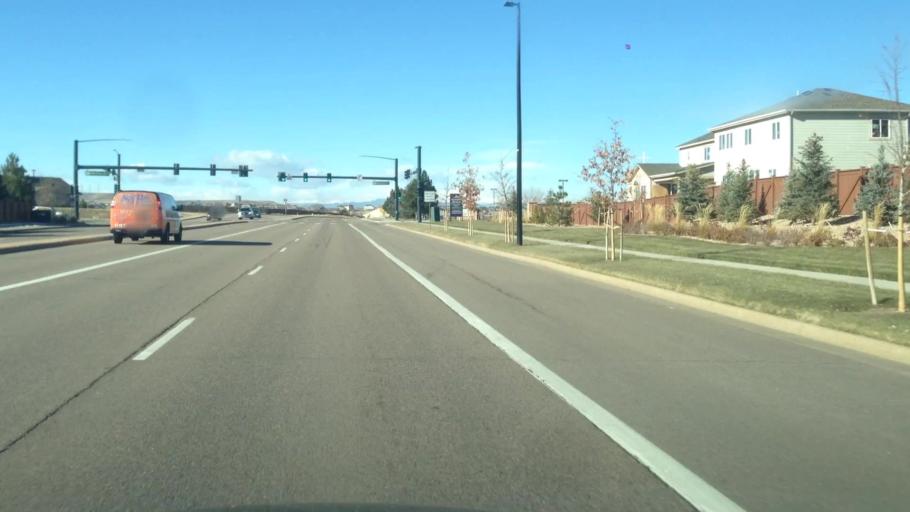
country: US
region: Colorado
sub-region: Douglas County
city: Stonegate
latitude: 39.5150
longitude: -104.8037
